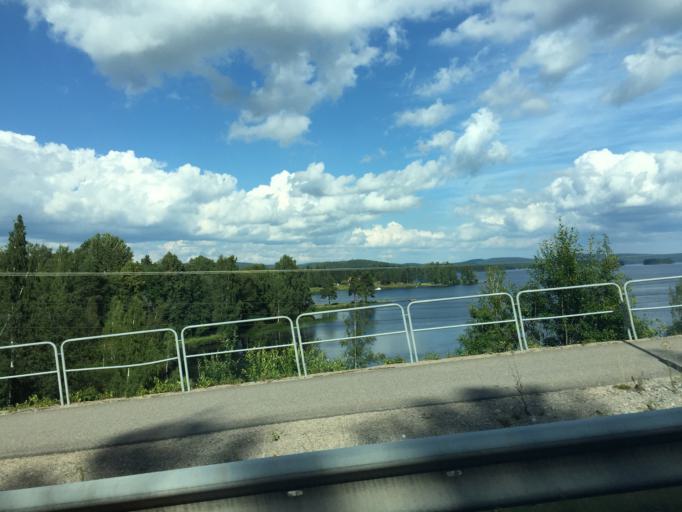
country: SE
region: Gaevleborg
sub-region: Bollnas Kommun
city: Kilafors
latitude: 61.2208
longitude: 16.5813
